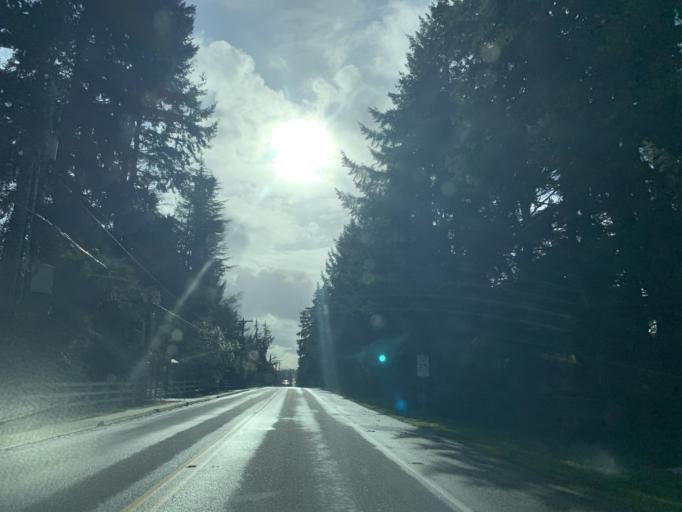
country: US
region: Washington
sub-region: King County
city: Lakeland South
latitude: 47.2709
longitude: -122.2978
